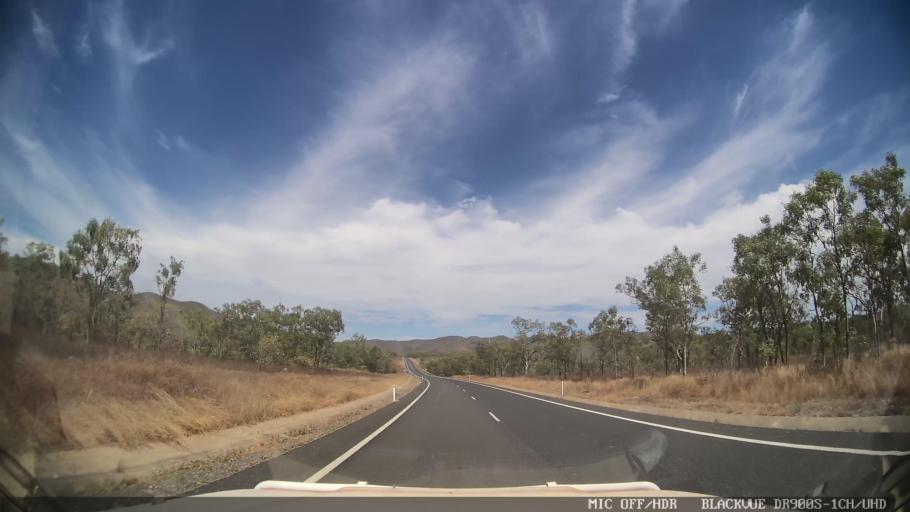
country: AU
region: Queensland
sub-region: Cook
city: Cooktown
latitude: -15.9350
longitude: 144.8389
